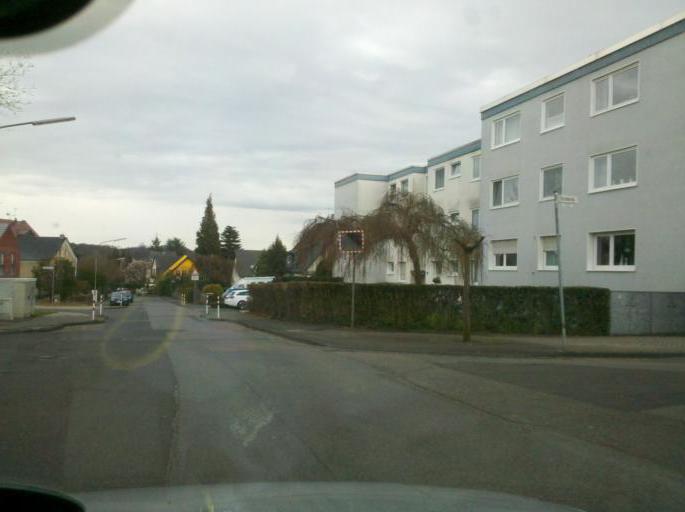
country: DE
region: North Rhine-Westphalia
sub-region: Regierungsbezirk Koln
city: Rosrath
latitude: 50.9002
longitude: 7.1753
